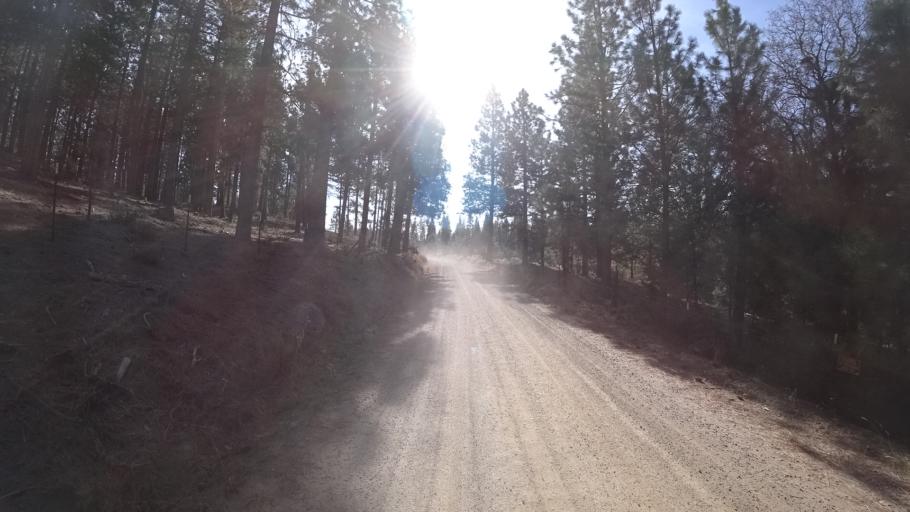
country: US
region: California
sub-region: Siskiyou County
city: Weed
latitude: 41.4353
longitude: -122.4237
